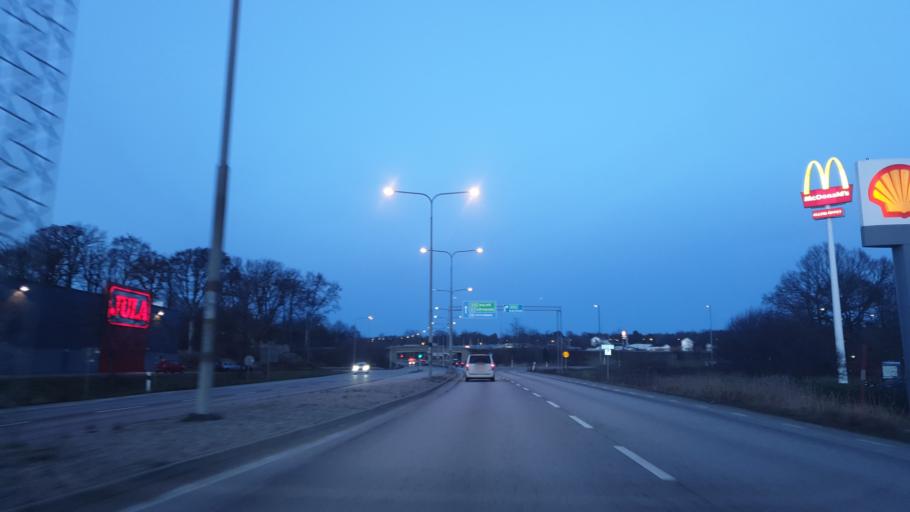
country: SE
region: Blekinge
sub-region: Karlskrona Kommun
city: Rodeby
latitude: 56.2039
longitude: 15.6400
